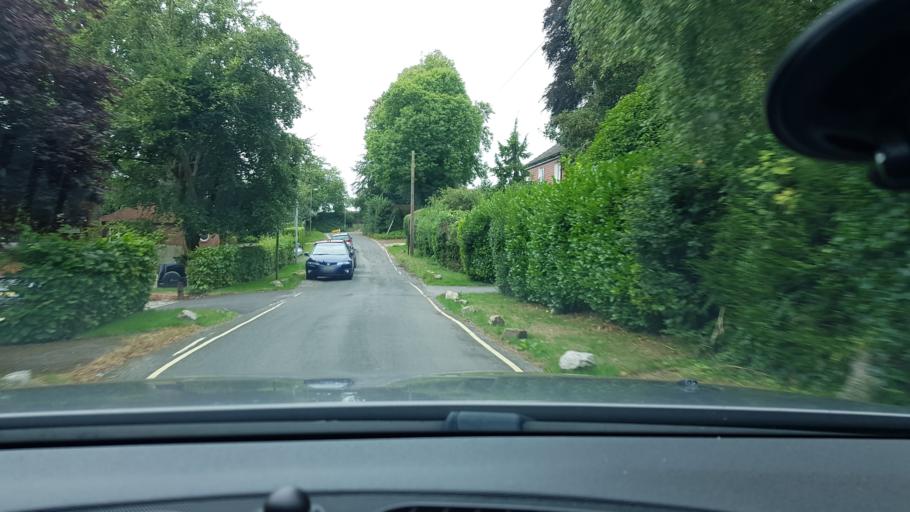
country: GB
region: England
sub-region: Wiltshire
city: Marlborough
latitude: 51.4222
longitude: -1.7349
